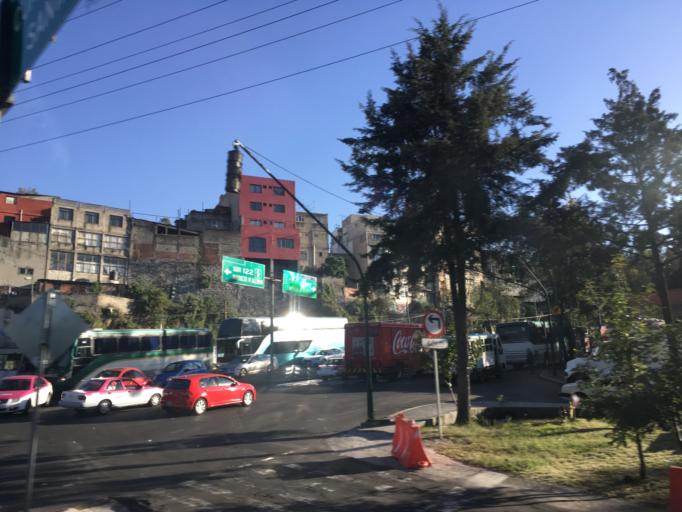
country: MX
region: Mexico City
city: Polanco
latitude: 19.3942
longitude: -99.1998
